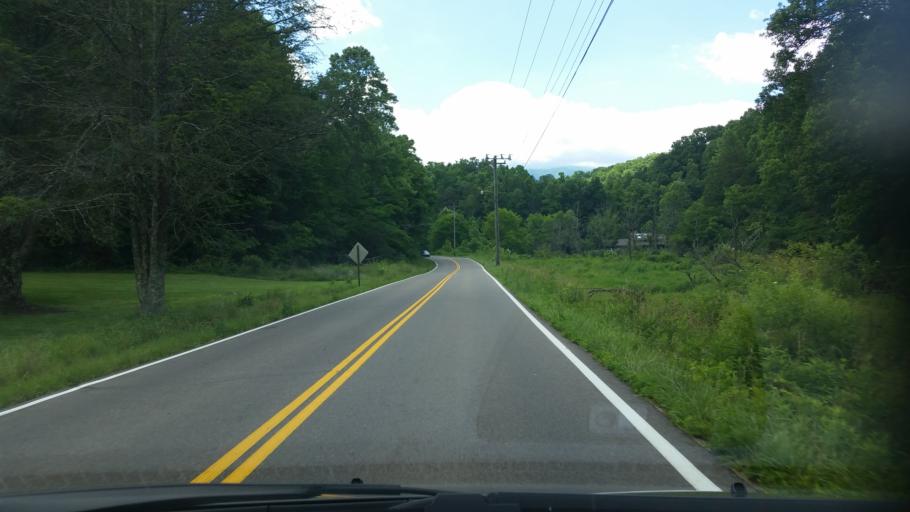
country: US
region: Tennessee
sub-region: Sevier County
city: Gatlinburg
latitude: 35.7549
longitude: -83.4372
